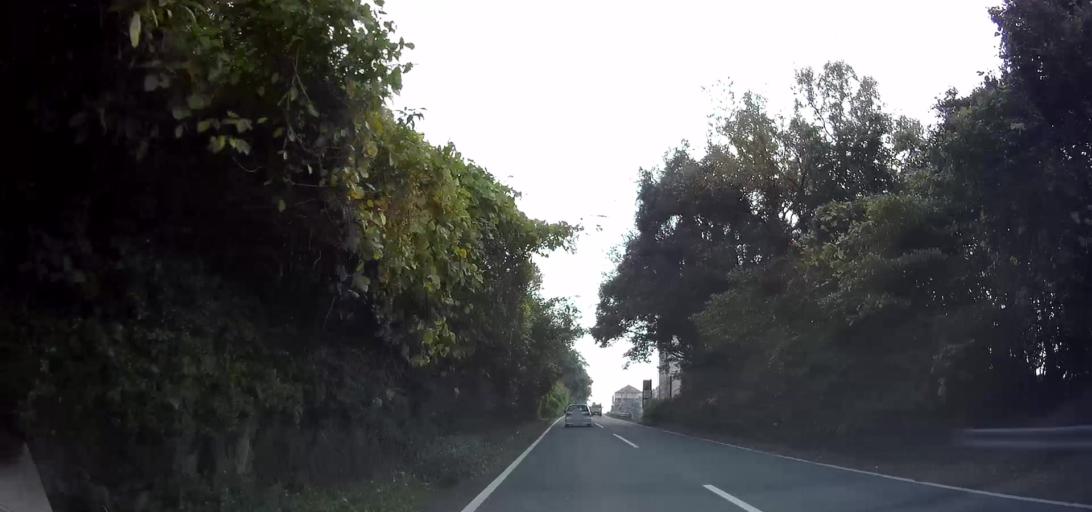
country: JP
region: Nagasaki
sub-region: Isahaya-shi
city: Isahaya
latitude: 32.7941
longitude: 130.1071
